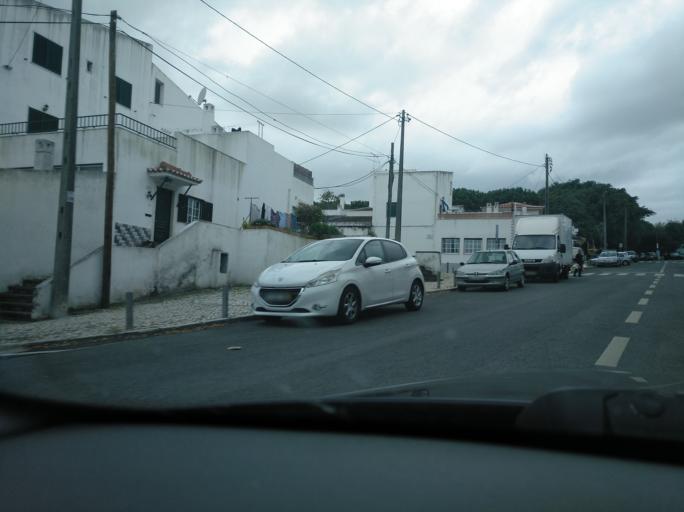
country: PT
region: Lisbon
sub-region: Amadora
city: Amadora
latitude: 38.7314
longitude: -9.2138
